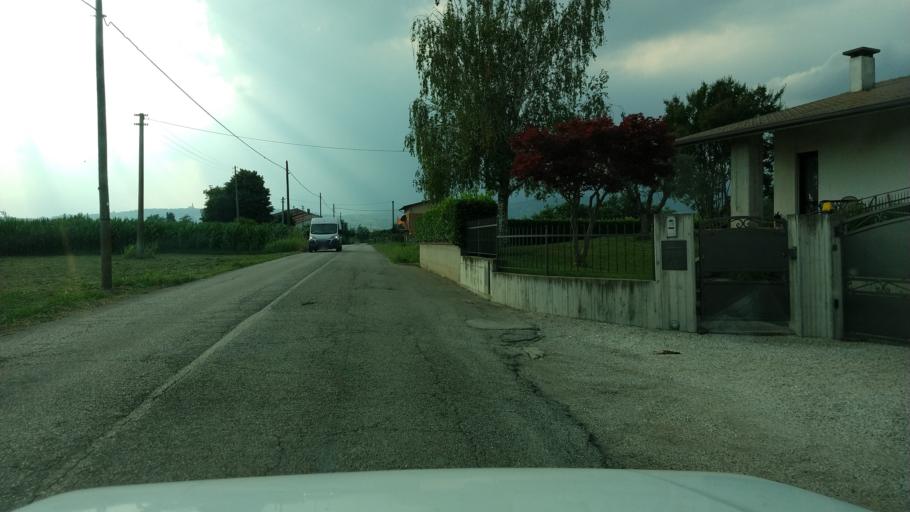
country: IT
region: Veneto
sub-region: Provincia di Vicenza
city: Schiavon
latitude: 45.7122
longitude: 11.6407
